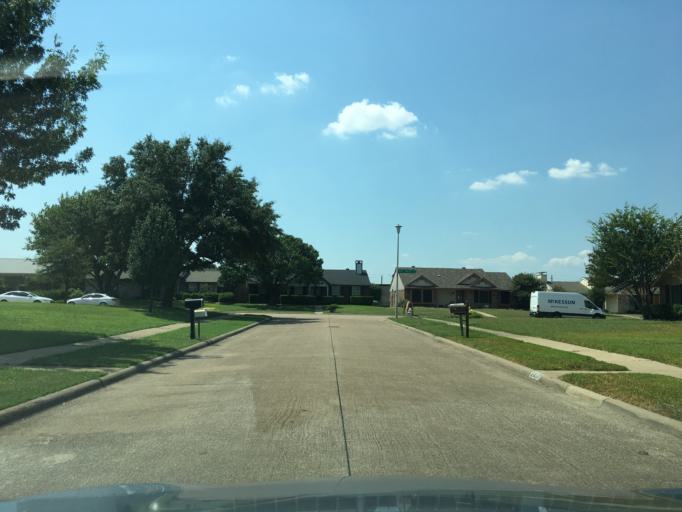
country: US
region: Texas
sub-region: Dallas County
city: Garland
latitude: 32.9476
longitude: -96.6627
